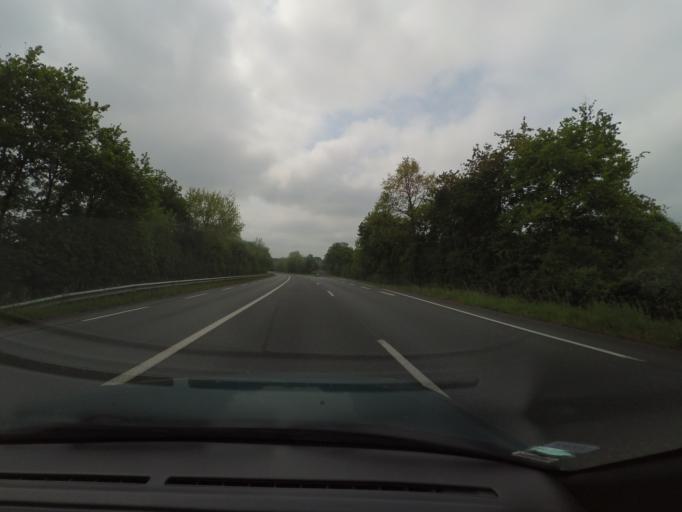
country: FR
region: Pays de la Loire
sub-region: Departement de la Vendee
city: Aubigny
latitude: 46.6079
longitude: -1.4454
